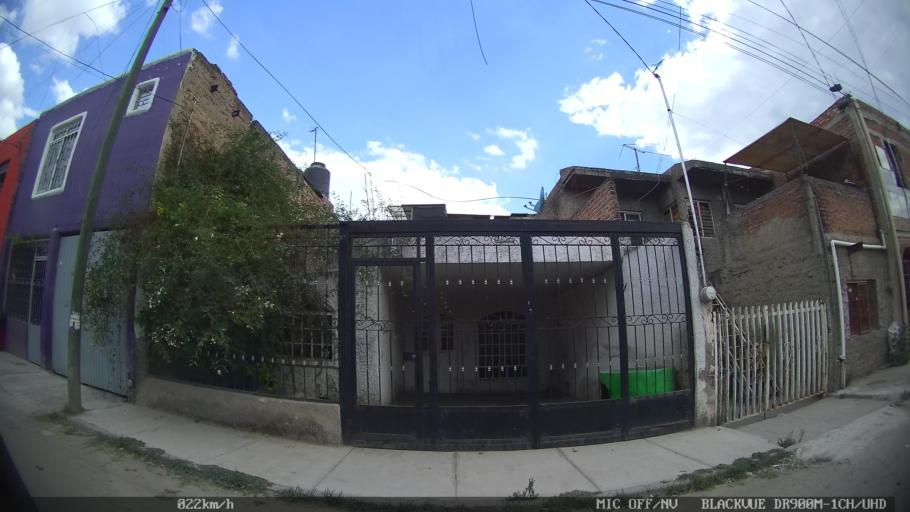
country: MX
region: Jalisco
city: Tonala
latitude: 20.6559
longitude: -103.2552
